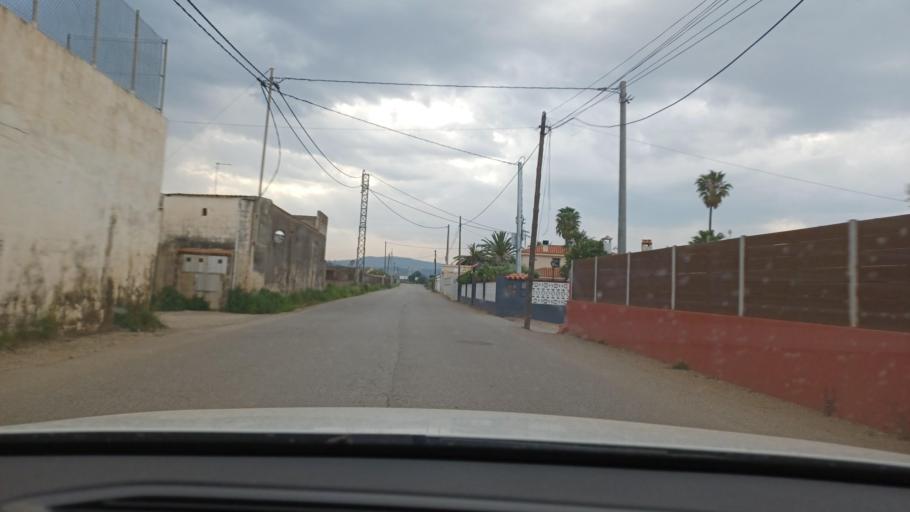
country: ES
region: Valencia
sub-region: Provincia de Castello
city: Benicarlo
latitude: 40.4062
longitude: 0.4015
